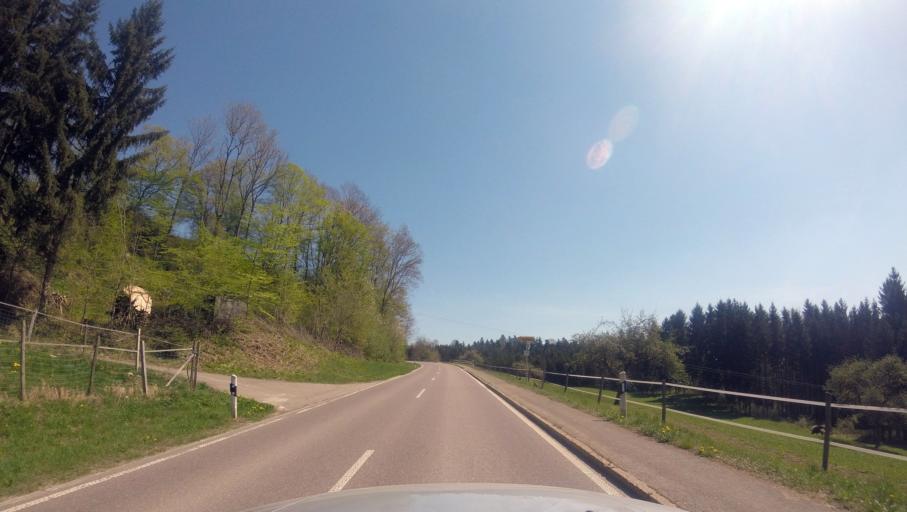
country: DE
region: Baden-Wuerttemberg
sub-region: Regierungsbezirk Stuttgart
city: Durlangen
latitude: 48.8495
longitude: 9.7799
